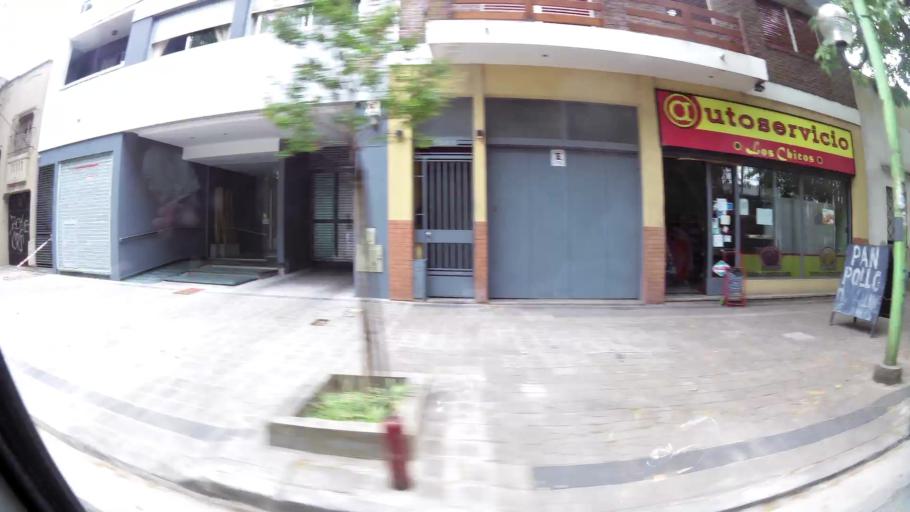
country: AR
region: Buenos Aires
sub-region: Partido de La Plata
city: La Plata
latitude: -34.9299
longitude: -57.9651
